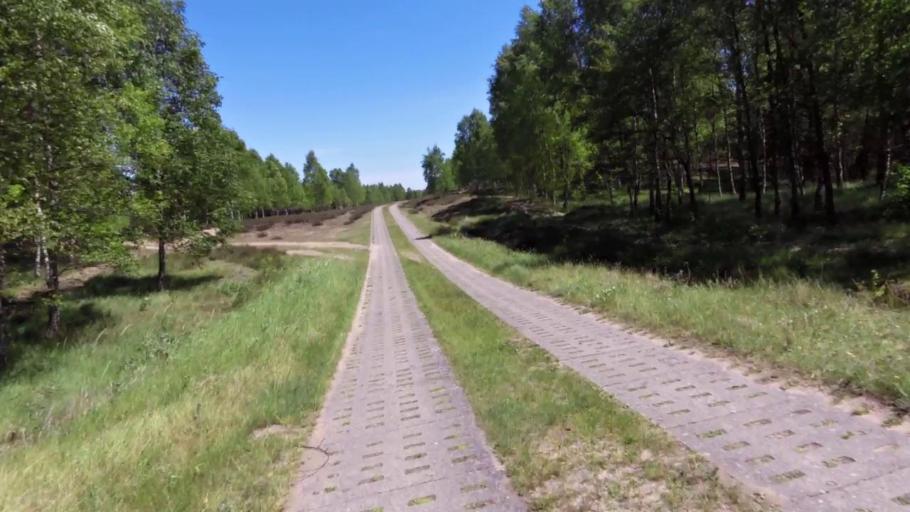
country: PL
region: West Pomeranian Voivodeship
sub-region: Powiat szczecinecki
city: Borne Sulinowo
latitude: 53.5728
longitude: 16.6343
